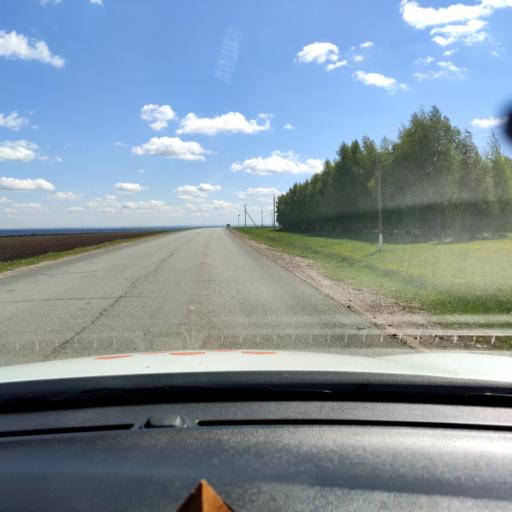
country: RU
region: Tatarstan
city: Verkhniy Uslon
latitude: 55.5562
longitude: 48.9132
